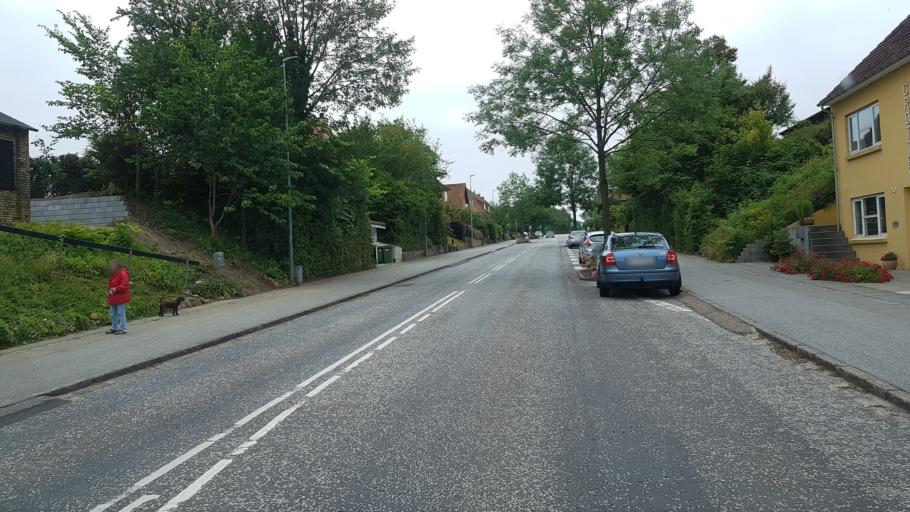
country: DK
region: Central Jutland
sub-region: Struer Kommune
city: Struer
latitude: 56.4890
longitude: 8.5956
